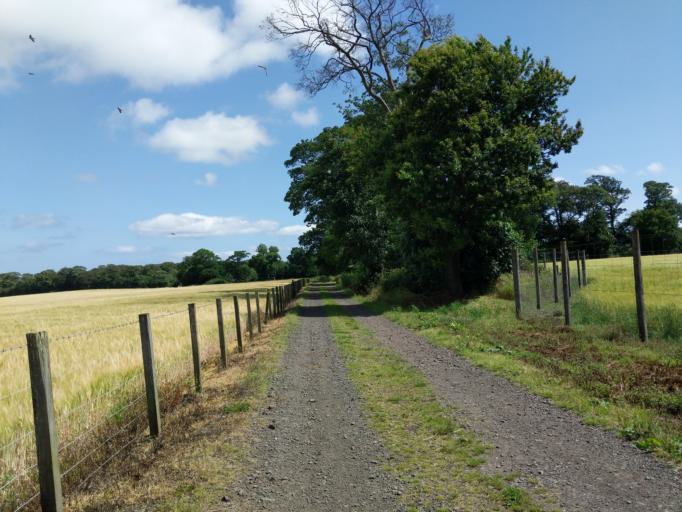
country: GB
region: Scotland
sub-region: Edinburgh
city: Ratho
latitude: 55.9288
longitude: -3.3375
